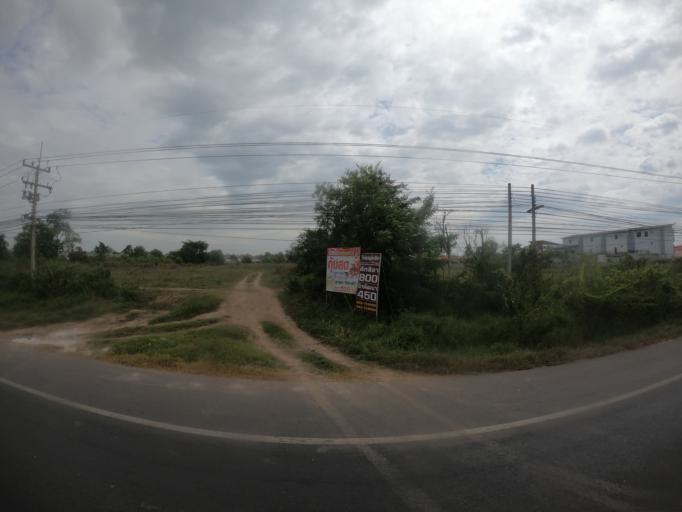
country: TH
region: Maha Sarakham
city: Maha Sarakham
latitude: 16.2523
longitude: 103.2760
